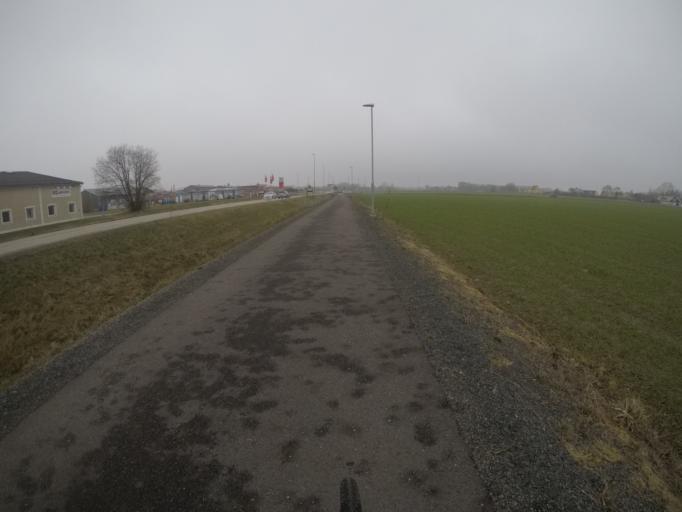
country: SE
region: Skane
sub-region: Hoganas Kommun
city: Hoganas
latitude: 56.2032
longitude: 12.5788
